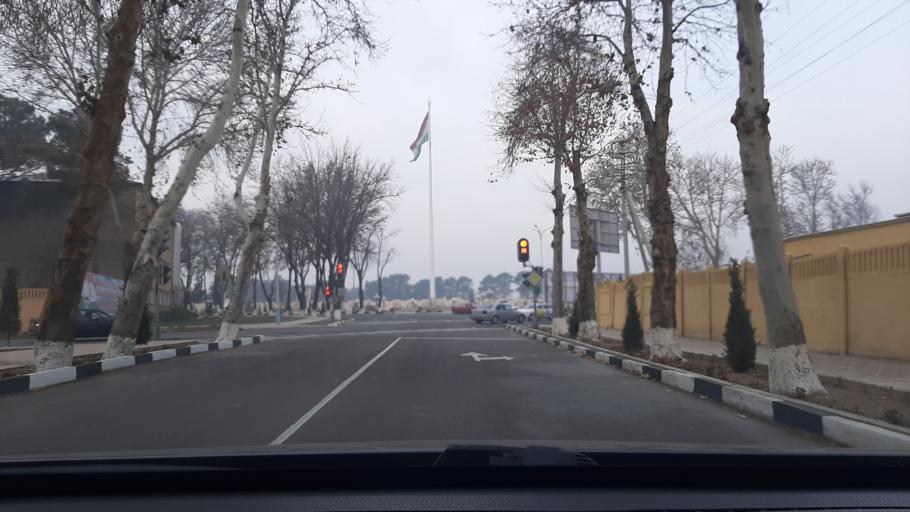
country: TJ
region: Viloyati Sughd
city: Chkalov
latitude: 40.2391
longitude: 69.6911
